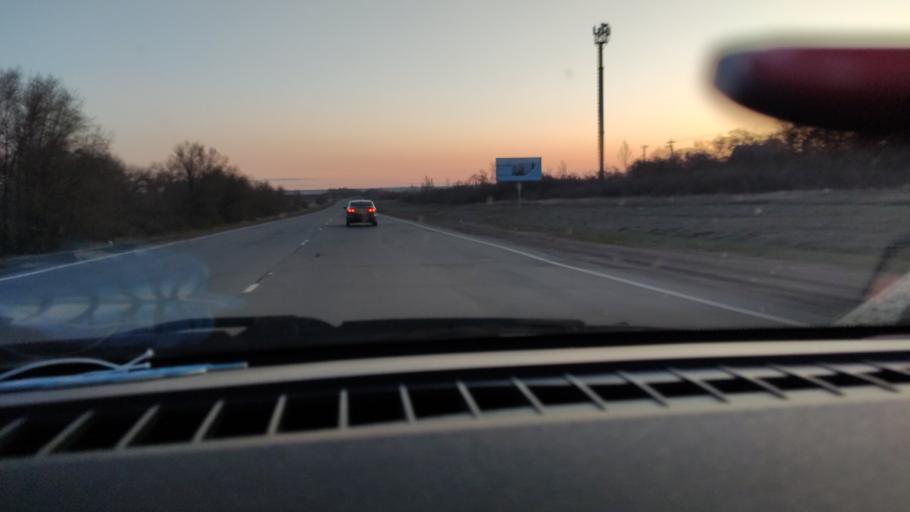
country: RU
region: Saratov
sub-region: Saratovskiy Rayon
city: Saratov
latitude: 51.6856
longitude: 46.0034
